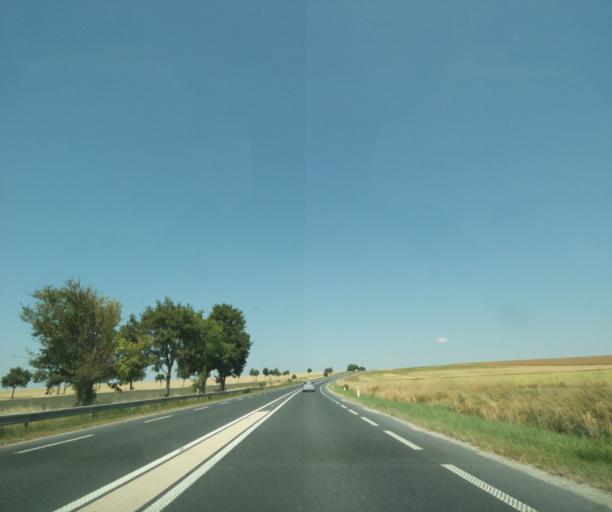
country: FR
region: Champagne-Ardenne
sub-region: Departement de la Marne
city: Mourmelon-le-Grand
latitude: 49.0717
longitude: 4.2913
